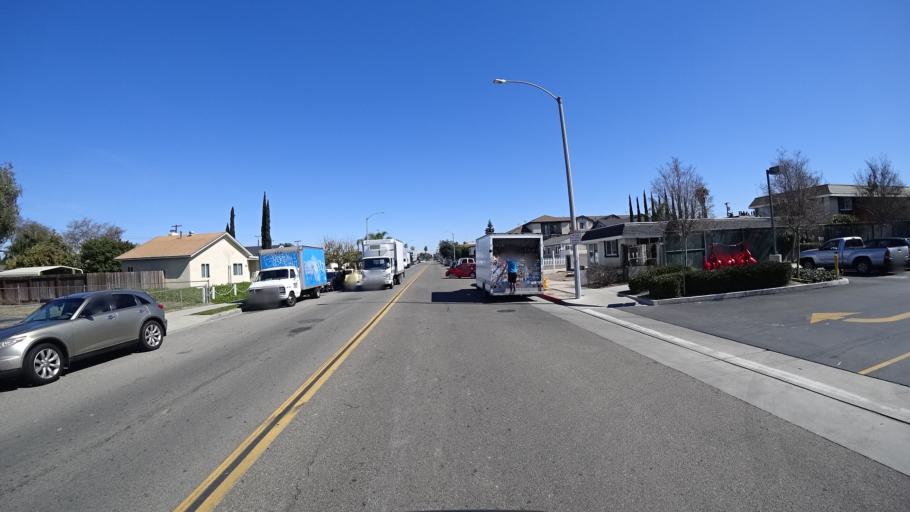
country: US
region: California
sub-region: Orange County
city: Anaheim
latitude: 33.8222
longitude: -117.9138
